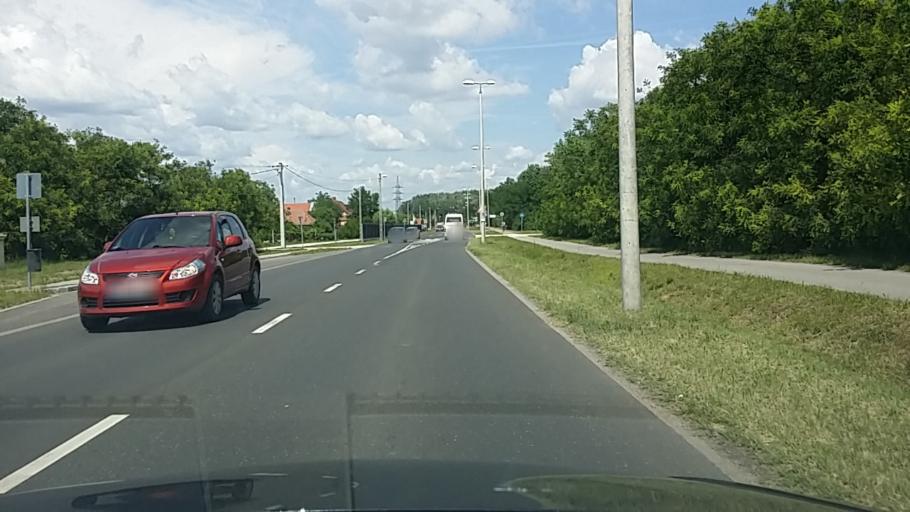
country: HU
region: Bacs-Kiskun
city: Kecskemet
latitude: 46.9014
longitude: 19.6454
